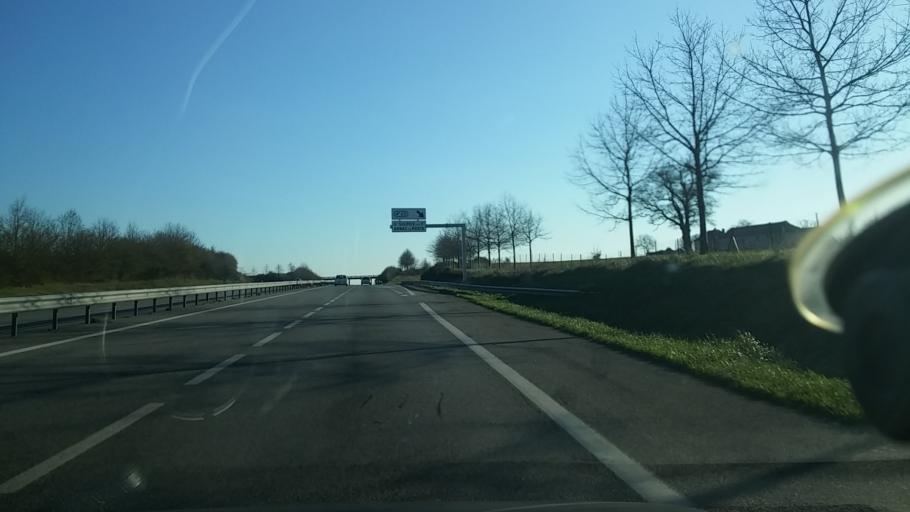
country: FR
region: Limousin
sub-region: Departement de la Haute-Vienne
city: Arnac-la-Poste
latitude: 46.2806
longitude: 1.4041
